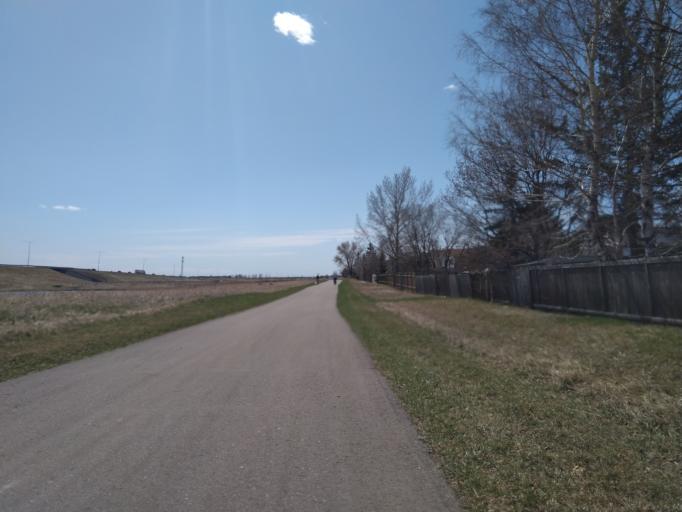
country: CA
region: Alberta
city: Chestermere
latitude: 51.0593
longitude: -113.9234
